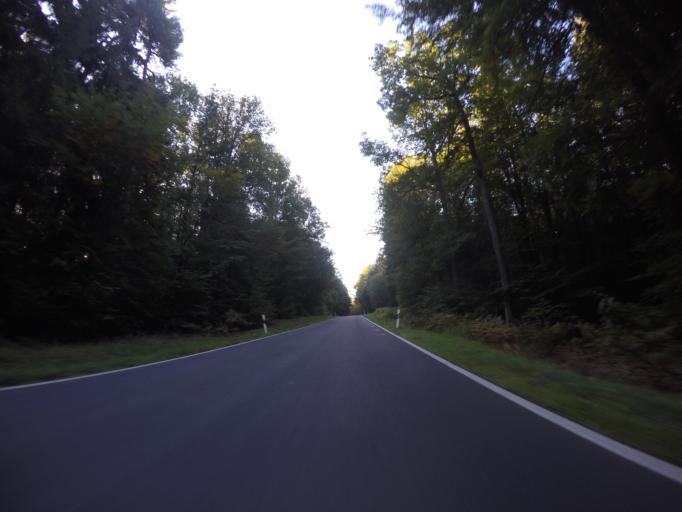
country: DE
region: Bavaria
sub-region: Regierungsbezirk Unterfranken
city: Altenbuch
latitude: 49.8782
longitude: 9.4030
